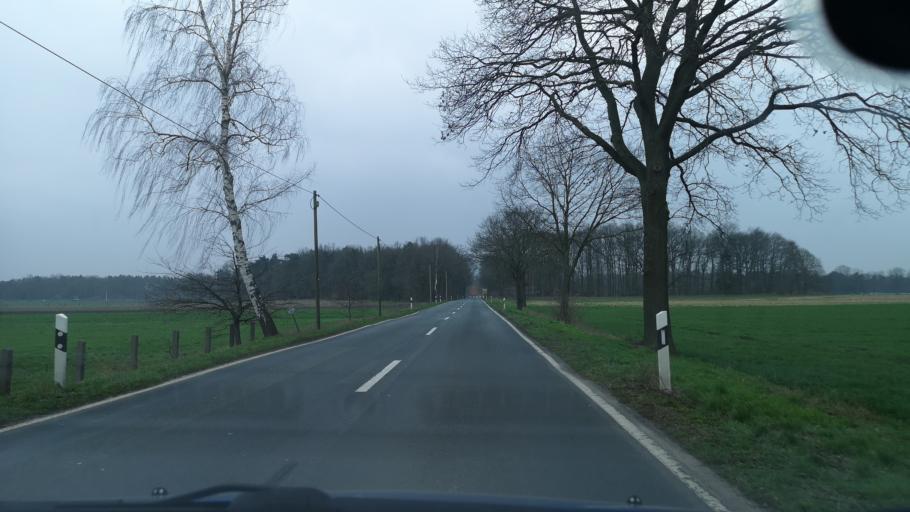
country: DE
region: Lower Saxony
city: Neustadt am Rubenberge
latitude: 52.5406
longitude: 9.4020
